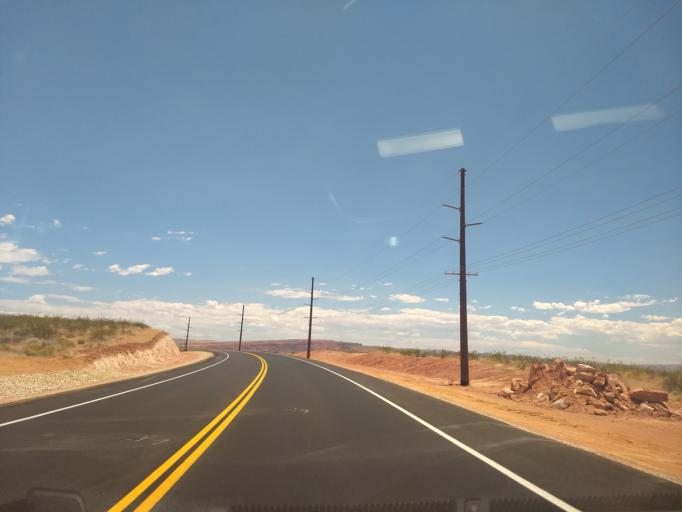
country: US
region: Utah
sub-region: Washington County
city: Washington
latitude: 37.1498
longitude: -113.5159
